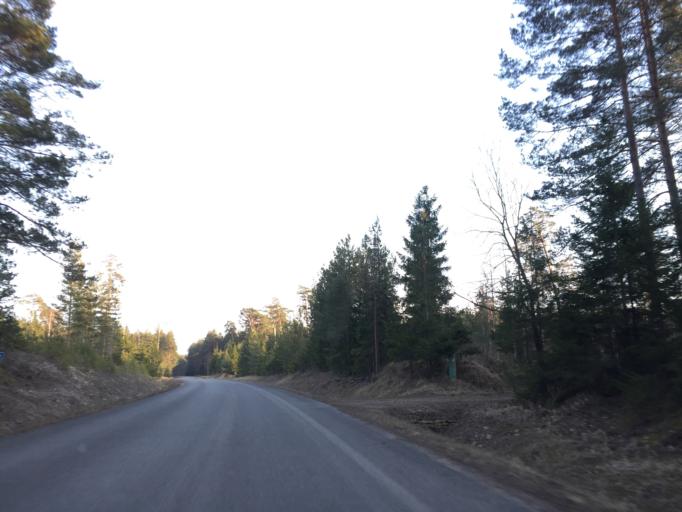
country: EE
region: Laeaene
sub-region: Lihula vald
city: Lihula
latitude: 58.4715
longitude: 23.7116
